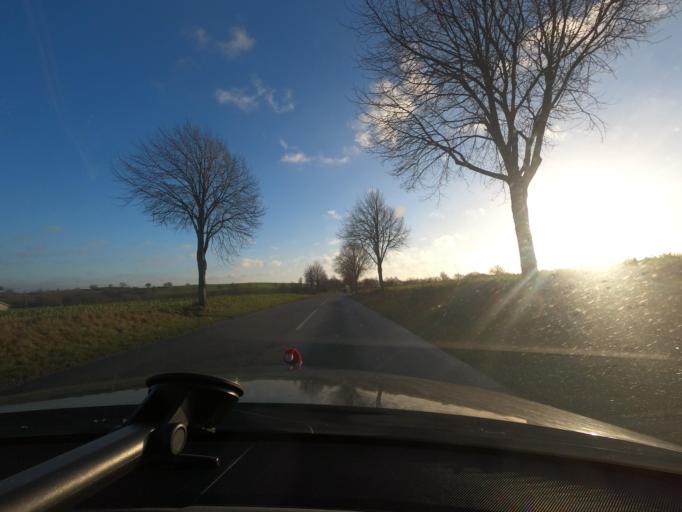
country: DK
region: South Denmark
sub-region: Sonderborg Kommune
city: Broager
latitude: 54.8942
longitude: 9.6843
